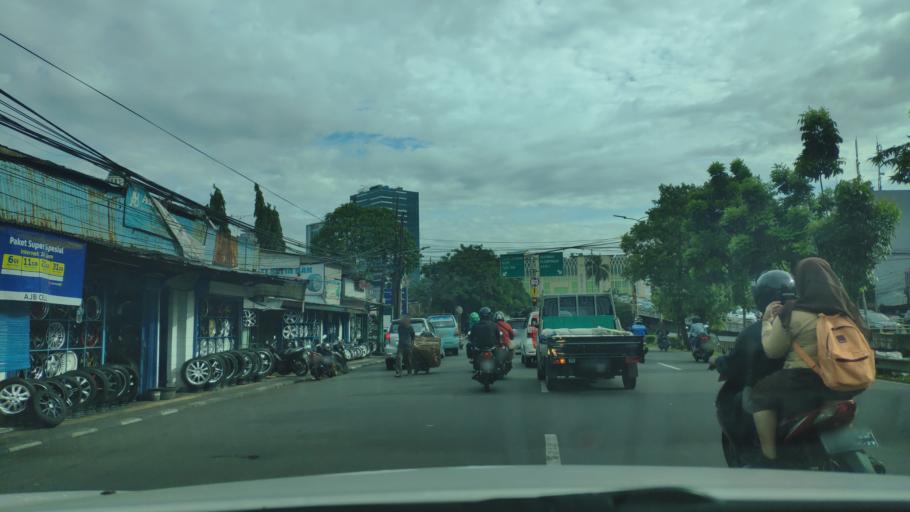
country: ID
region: Jakarta Raya
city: Jakarta
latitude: -6.1799
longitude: 106.8132
